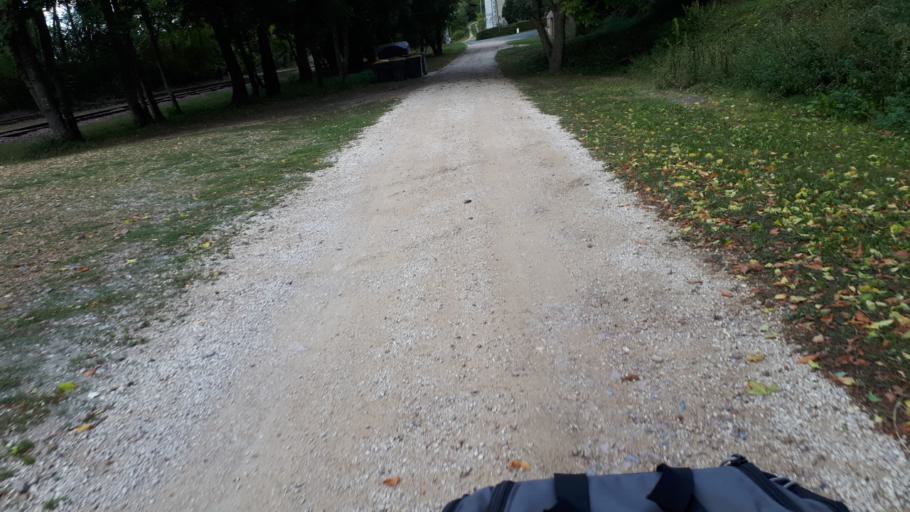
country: FR
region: Centre
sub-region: Departement du Loir-et-Cher
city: Villiers-sur-Loir
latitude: 47.7756
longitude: 0.9629
